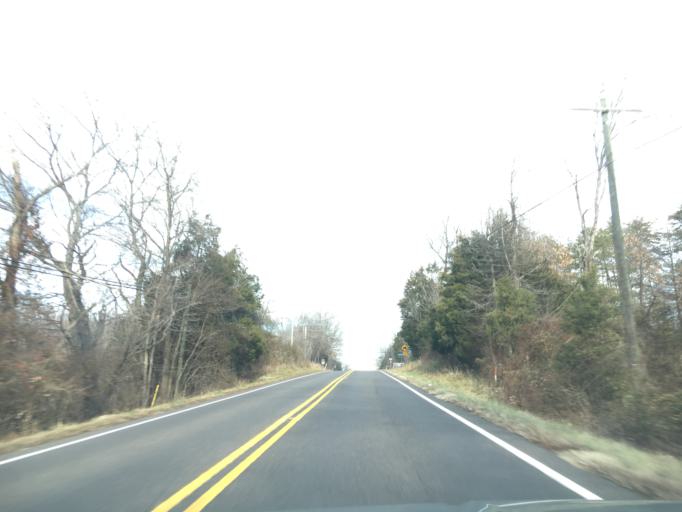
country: US
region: Virginia
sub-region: Culpeper County
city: Culpeper
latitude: 38.5715
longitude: -77.9815
